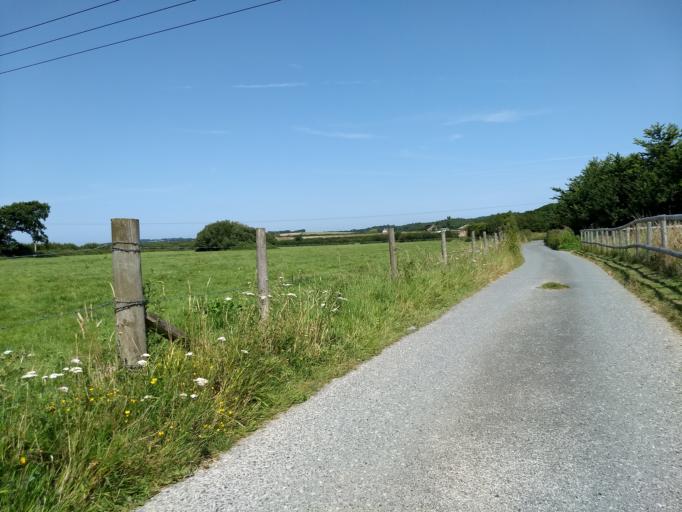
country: GB
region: England
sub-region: Isle of Wight
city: Newport
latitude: 50.6984
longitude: -1.3380
